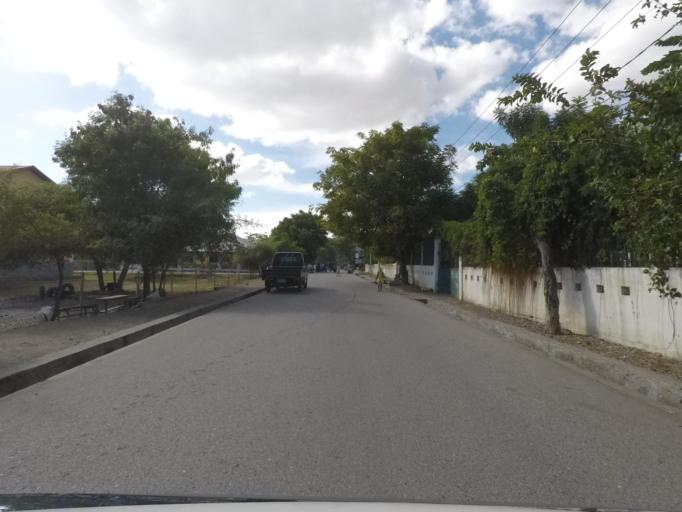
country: TL
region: Manatuto
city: Manatuto
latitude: -8.5102
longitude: 126.0145
